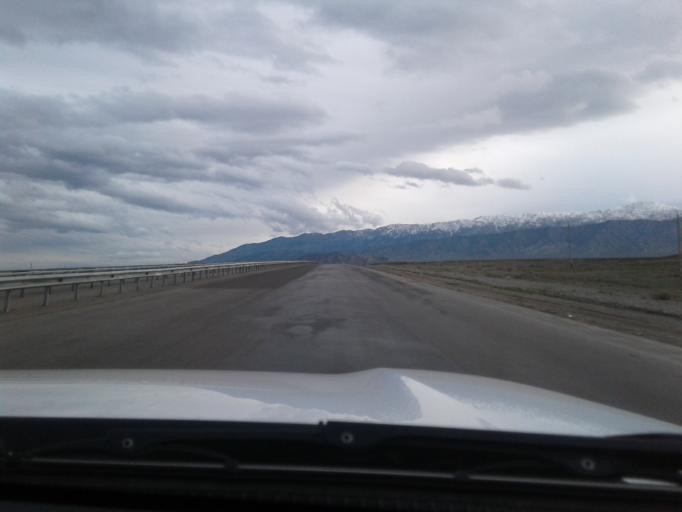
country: TM
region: Ahal
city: Baharly
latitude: 38.5712
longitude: 57.1254
